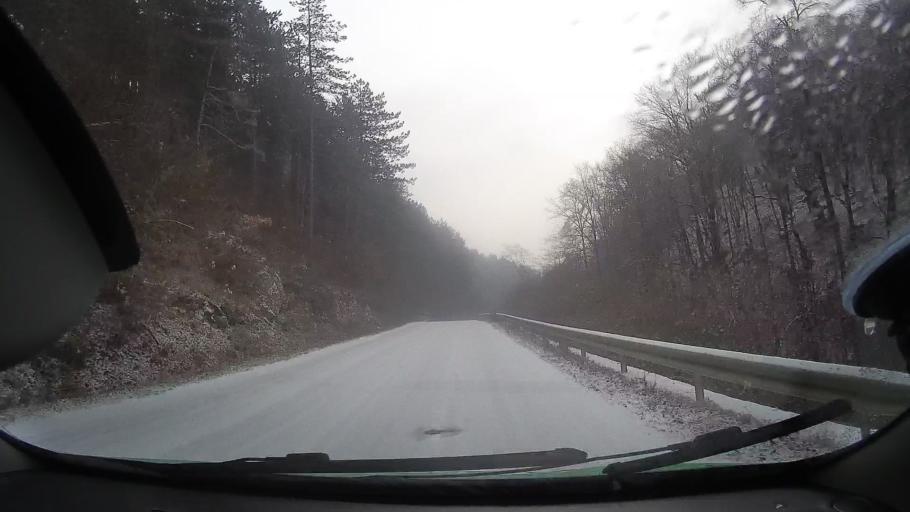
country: RO
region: Alba
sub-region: Comuna Livezile
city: Livezile
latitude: 46.3733
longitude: 23.5861
